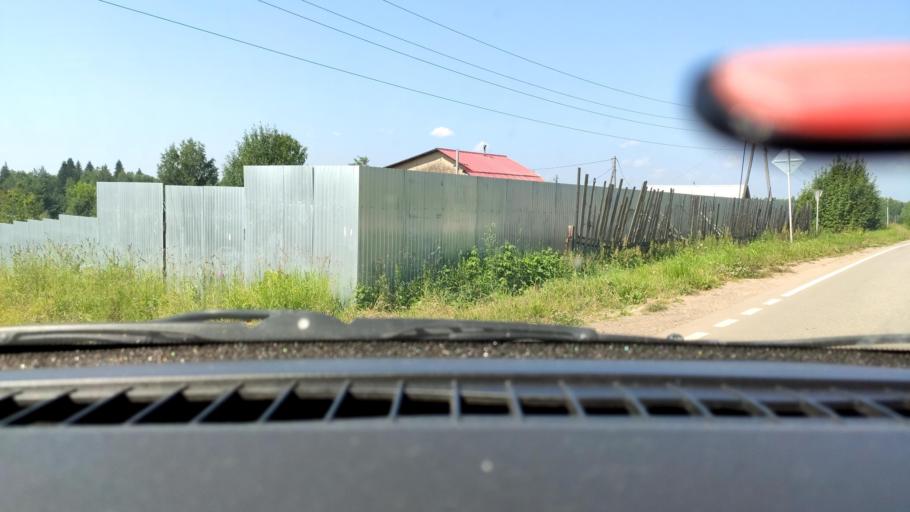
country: RU
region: Perm
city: Overyata
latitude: 58.1215
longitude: 55.8164
